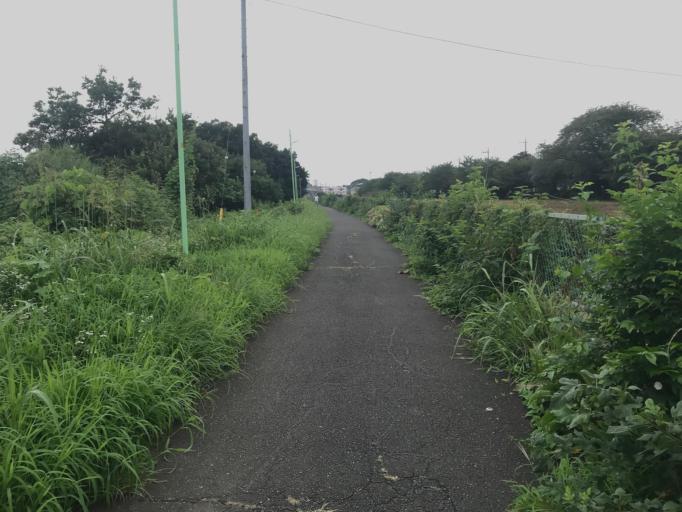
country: JP
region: Tokyo
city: Tanashicho
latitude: 35.7732
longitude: 139.5597
